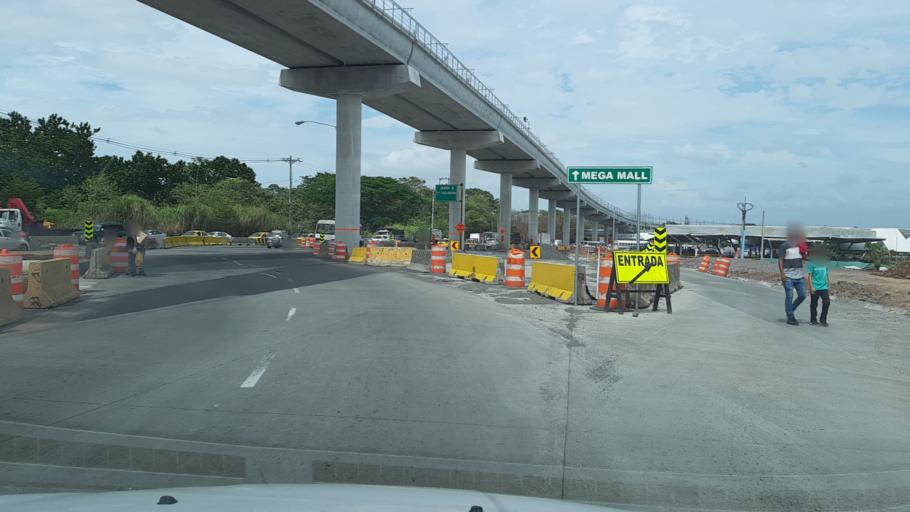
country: PA
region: Panama
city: Cabra Numero Uno
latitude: 9.1016
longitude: -79.3521
